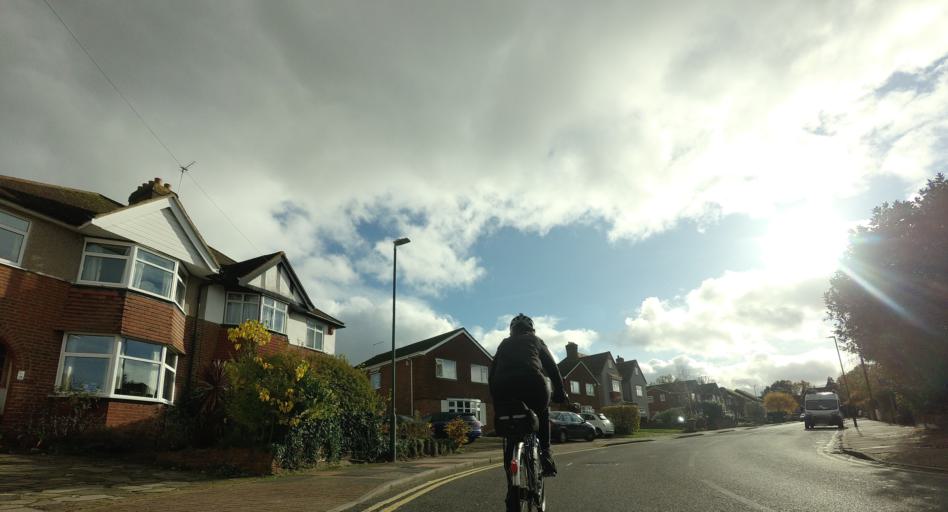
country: GB
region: England
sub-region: Greater London
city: Sidcup
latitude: 51.4319
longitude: 0.1134
